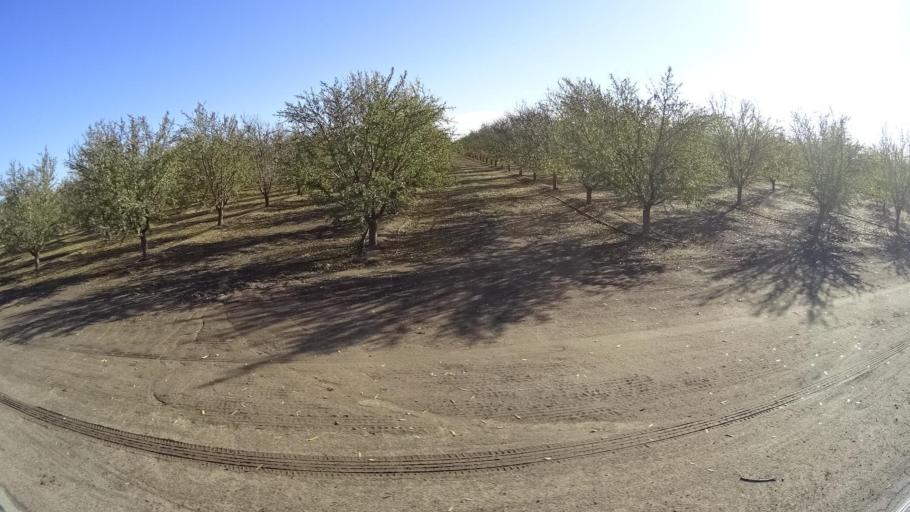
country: US
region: California
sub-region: Kern County
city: Delano
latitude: 35.7210
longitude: -119.3119
